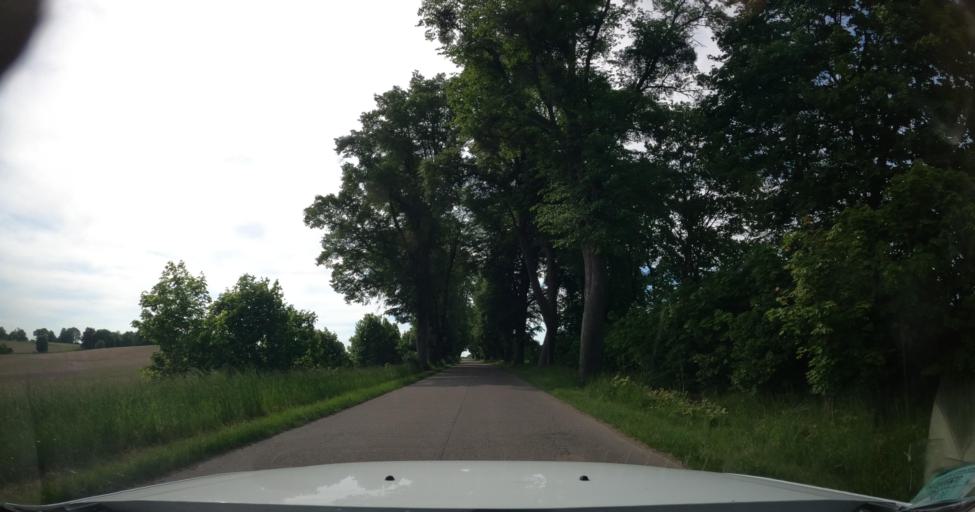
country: PL
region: Warmian-Masurian Voivodeship
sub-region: Powiat ostrodzki
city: Milakowo
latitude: 54.0168
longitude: 20.0540
